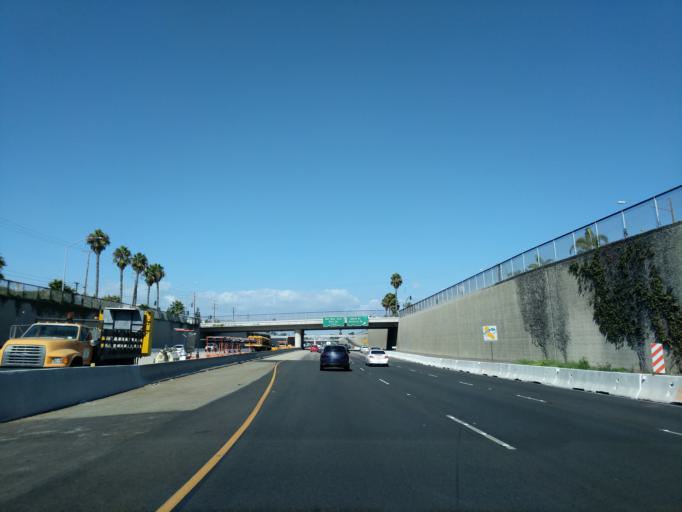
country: US
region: California
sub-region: Orange County
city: Costa Mesa
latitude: 33.6467
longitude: -117.9135
